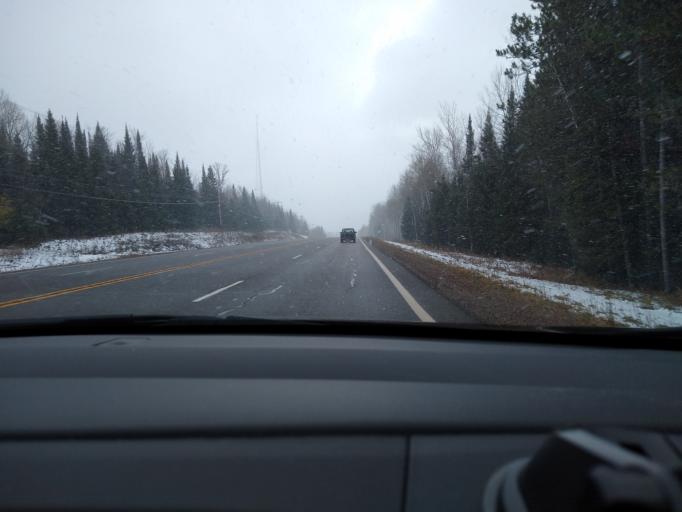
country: US
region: Wisconsin
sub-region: Florence County
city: Florence
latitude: 46.0480
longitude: -88.0624
